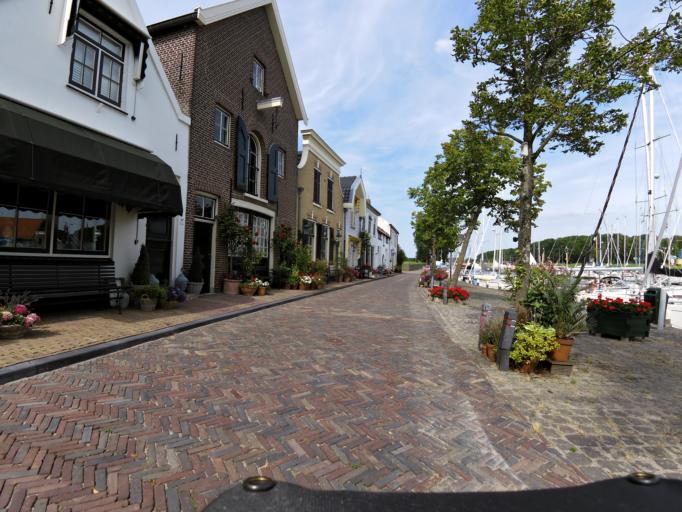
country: NL
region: South Holland
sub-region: Gemeente Goeree-Overflakkee
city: Middelharnis
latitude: 51.7608
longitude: 4.1667
